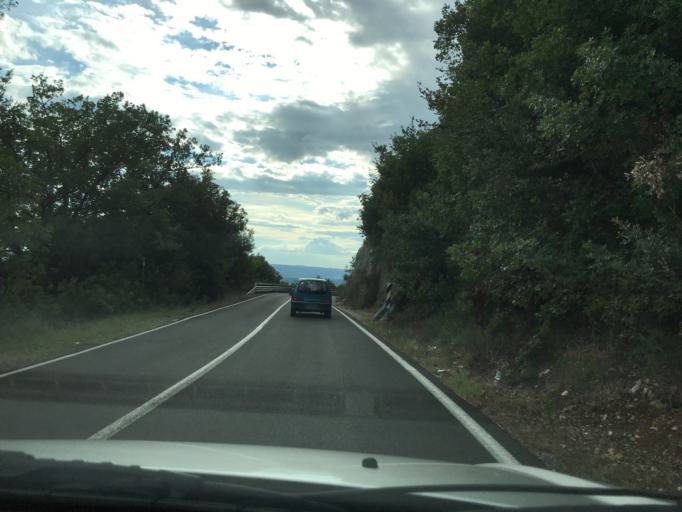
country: IT
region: Umbria
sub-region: Provincia di Terni
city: Guardea
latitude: 42.6318
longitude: 12.2943
